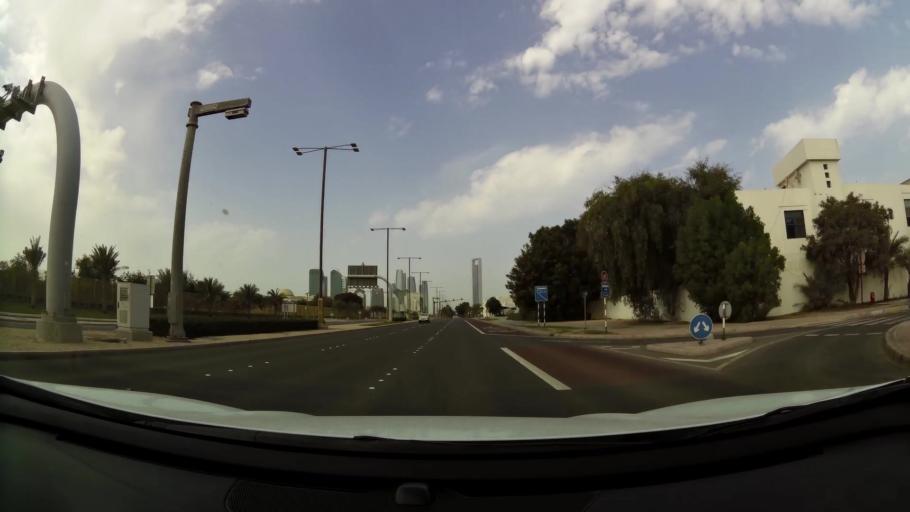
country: AE
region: Abu Dhabi
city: Abu Dhabi
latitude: 24.4548
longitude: 54.3487
